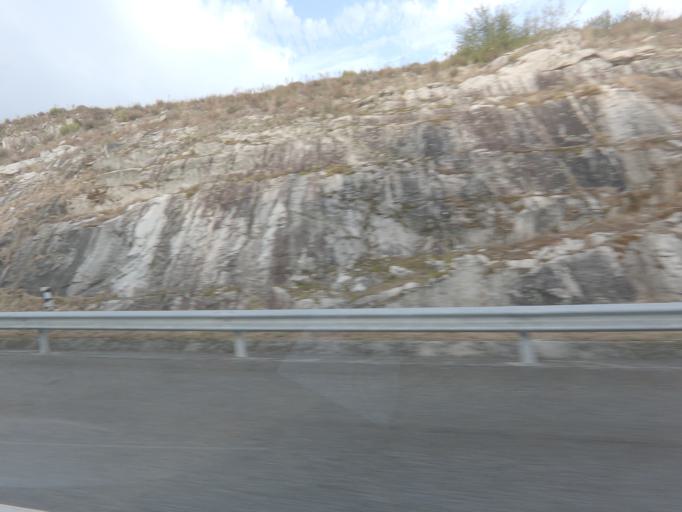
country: PT
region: Viseu
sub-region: Castro Daire
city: Castro Daire
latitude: 40.8300
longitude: -7.9368
